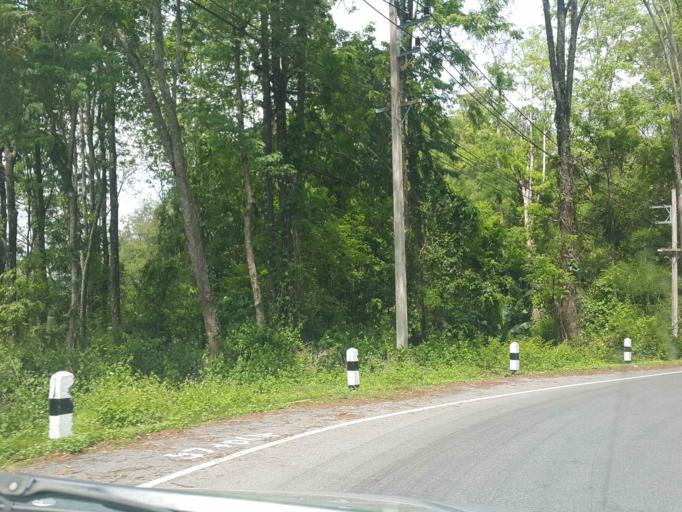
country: TH
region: Nan
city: Ban Luang
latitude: 18.8743
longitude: 100.4979
